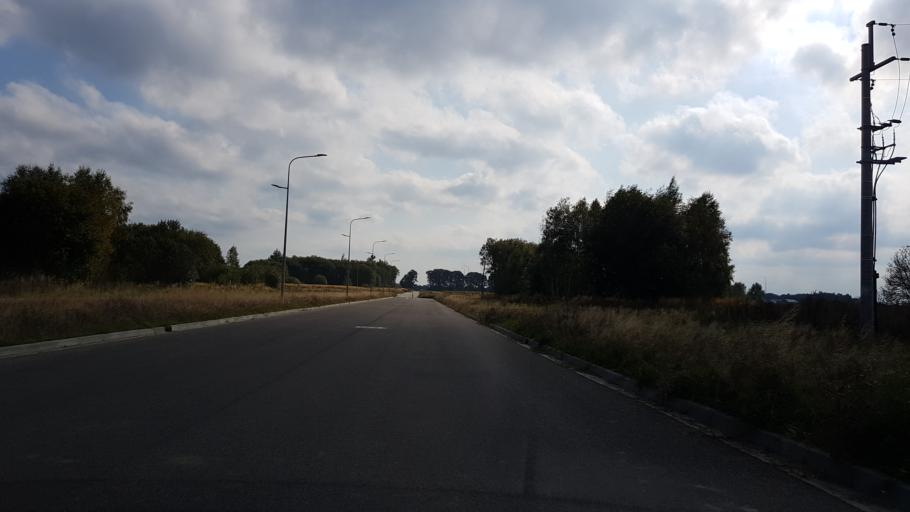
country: PL
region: West Pomeranian Voivodeship
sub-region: Koszalin
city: Koszalin
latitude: 54.1788
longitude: 16.1543
